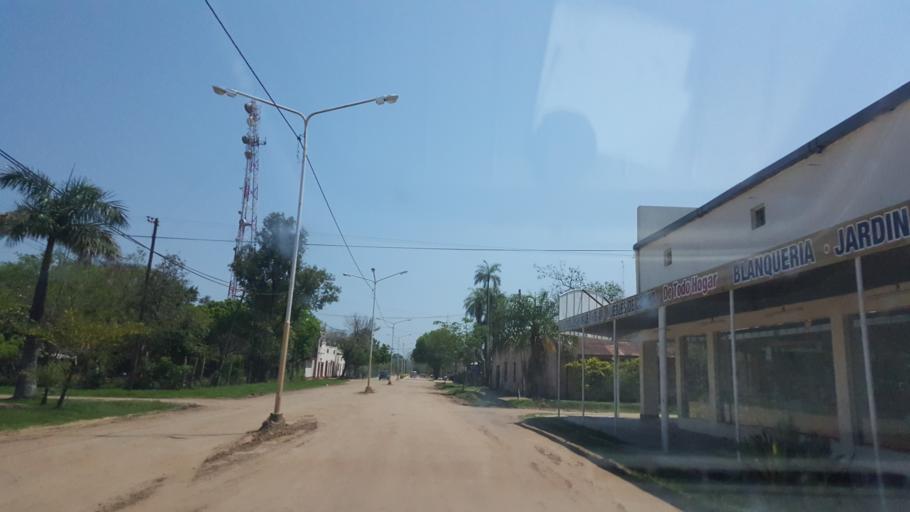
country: AR
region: Corrientes
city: Ita Ibate
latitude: -27.4258
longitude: -57.3351
